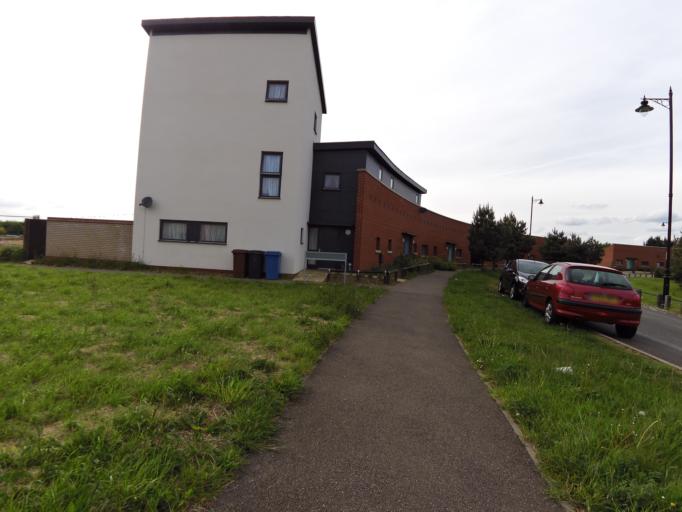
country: GB
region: England
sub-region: Suffolk
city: Ipswich
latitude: 52.0267
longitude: 1.1917
